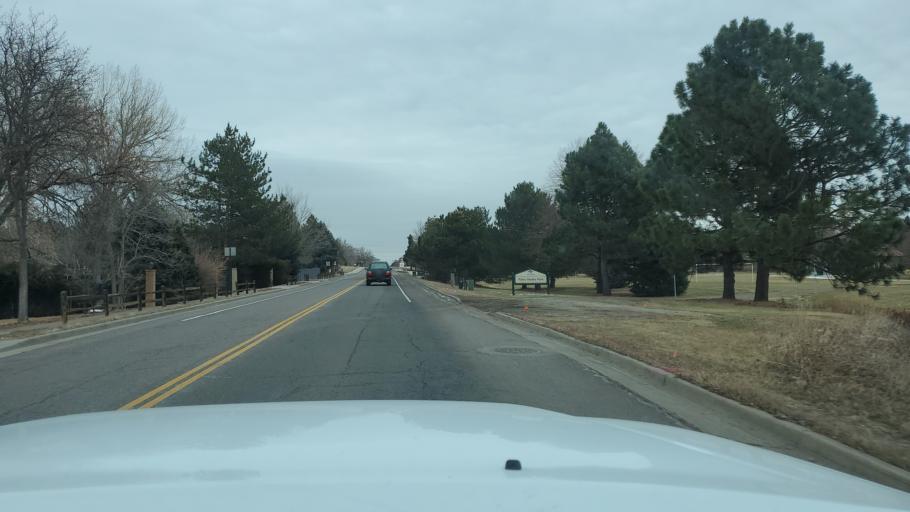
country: US
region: Colorado
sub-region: Arapahoe County
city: Castlewood
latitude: 39.6095
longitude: -104.9155
